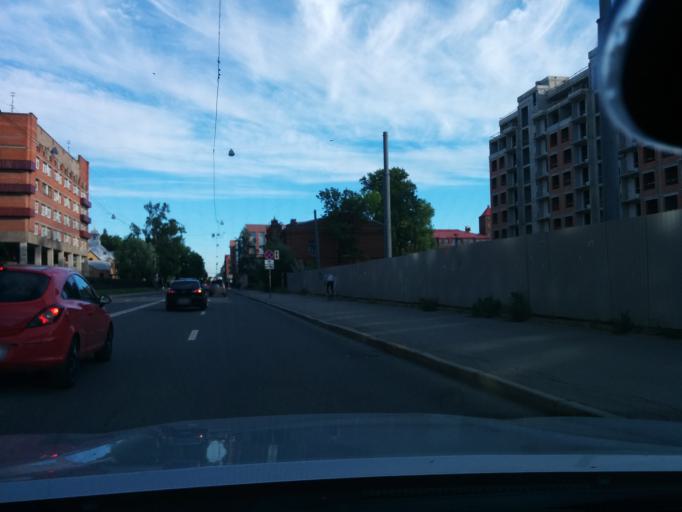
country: RU
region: Leningrad
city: Sampsonievskiy
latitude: 59.9786
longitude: 30.3375
